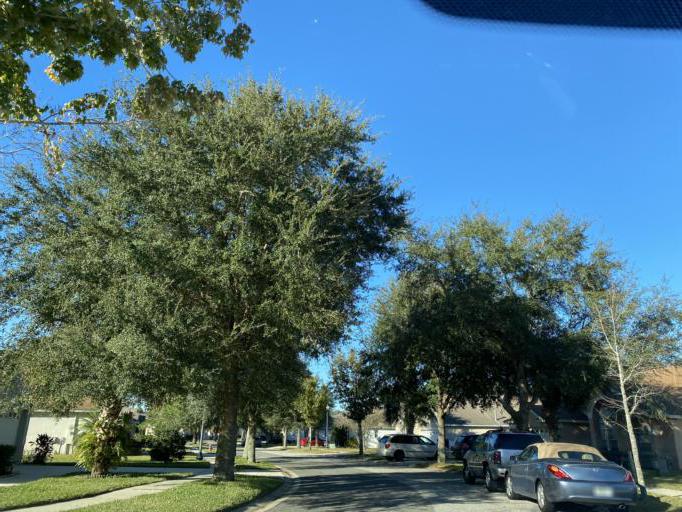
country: US
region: Florida
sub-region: Lake County
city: Four Corners
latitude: 28.3954
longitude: -81.6911
